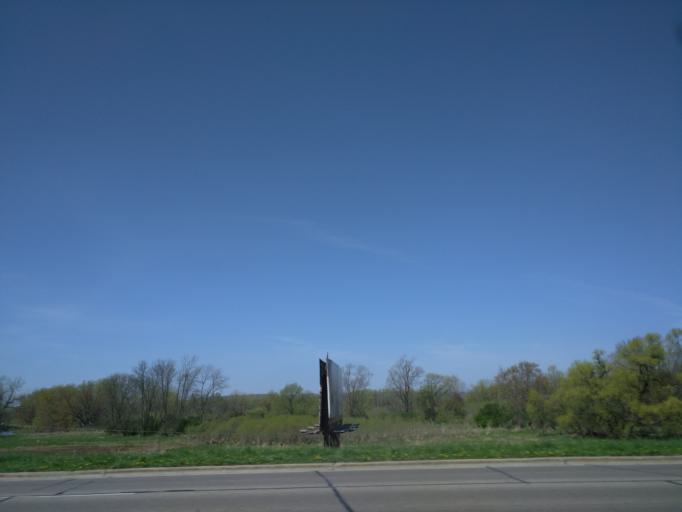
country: US
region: Wisconsin
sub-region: La Crosse County
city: North La Crosse
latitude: 43.8496
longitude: -91.2124
